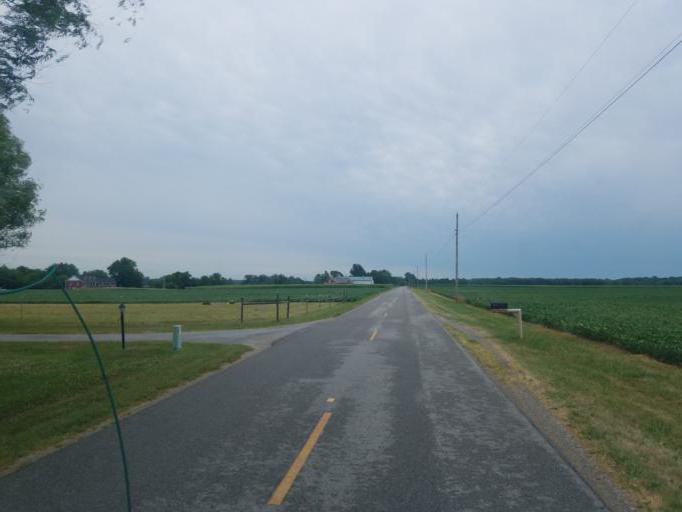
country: US
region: Ohio
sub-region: Paulding County
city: Antwerp
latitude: 41.2373
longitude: -84.7352
